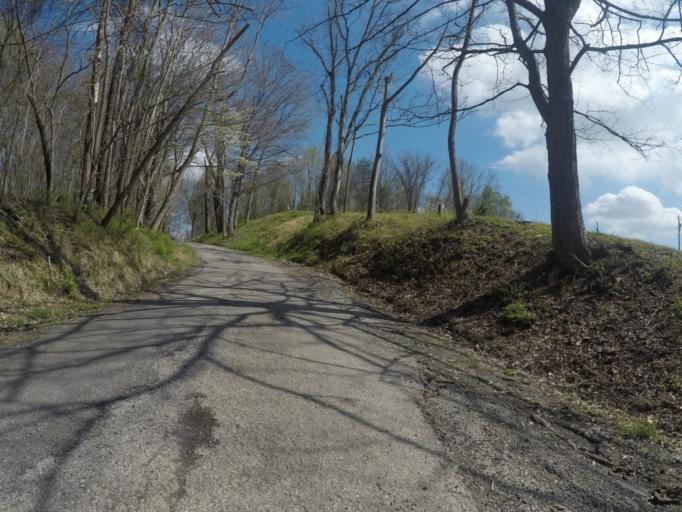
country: US
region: West Virginia
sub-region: Wayne County
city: Ceredo
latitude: 38.3876
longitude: -82.5436
